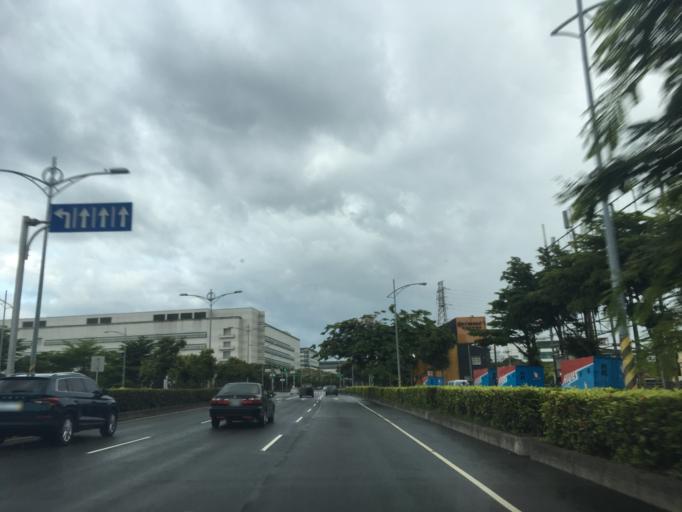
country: TW
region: Taiwan
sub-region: Taichung City
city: Taichung
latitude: 24.2067
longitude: 120.6266
